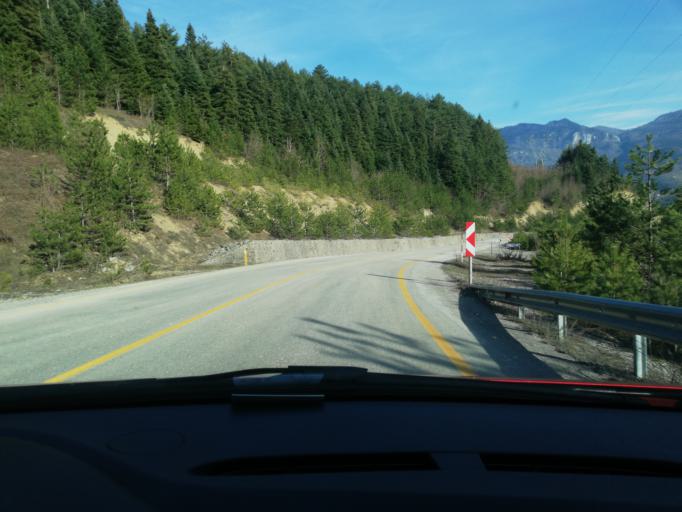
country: TR
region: Kastamonu
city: Senpazar
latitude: 41.7876
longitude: 33.1571
